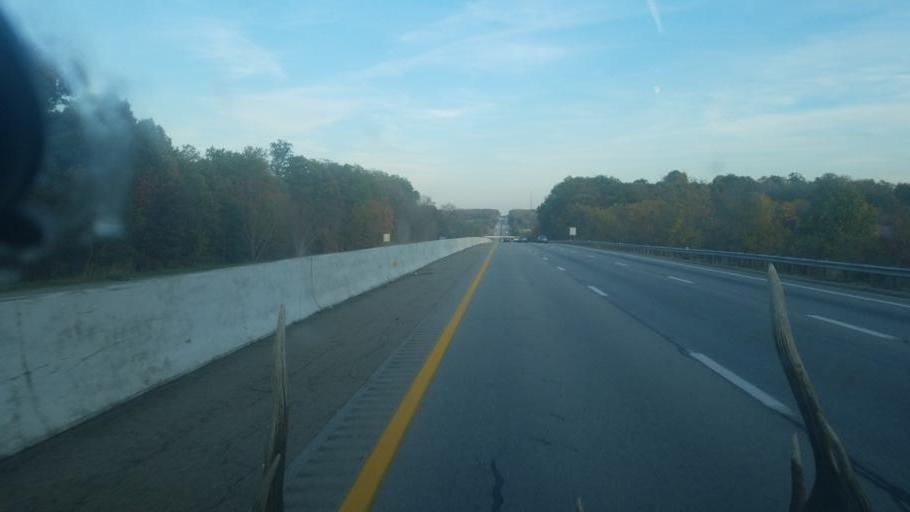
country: US
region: Ohio
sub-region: Perry County
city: Thornport
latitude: 39.9407
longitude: -82.3531
